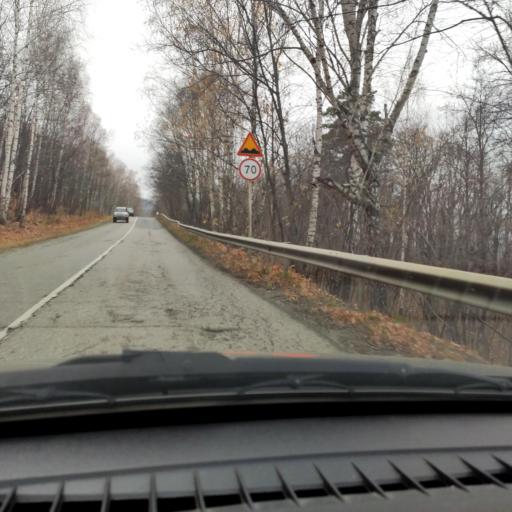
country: RU
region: Samara
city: Pribrezhnyy
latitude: 53.4395
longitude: 49.7404
